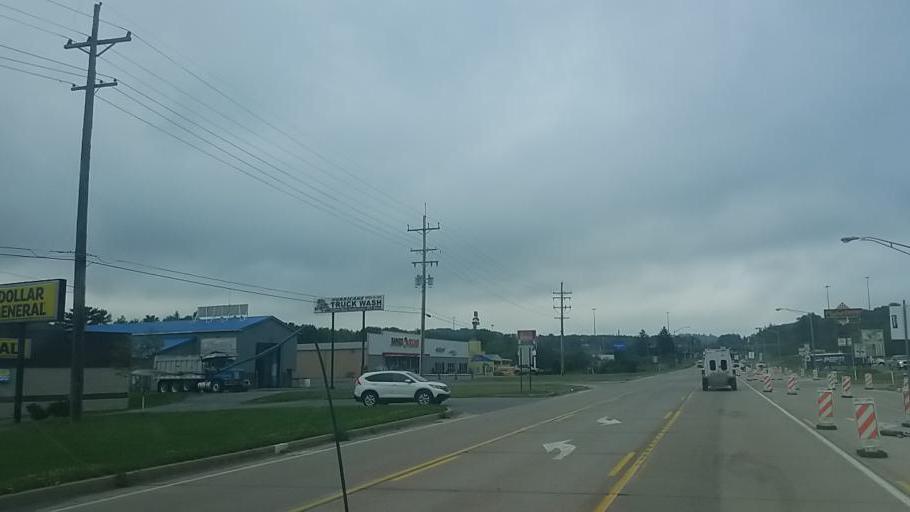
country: US
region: Pennsylvania
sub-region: Jefferson County
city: Brookville
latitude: 41.1661
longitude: -79.0977
